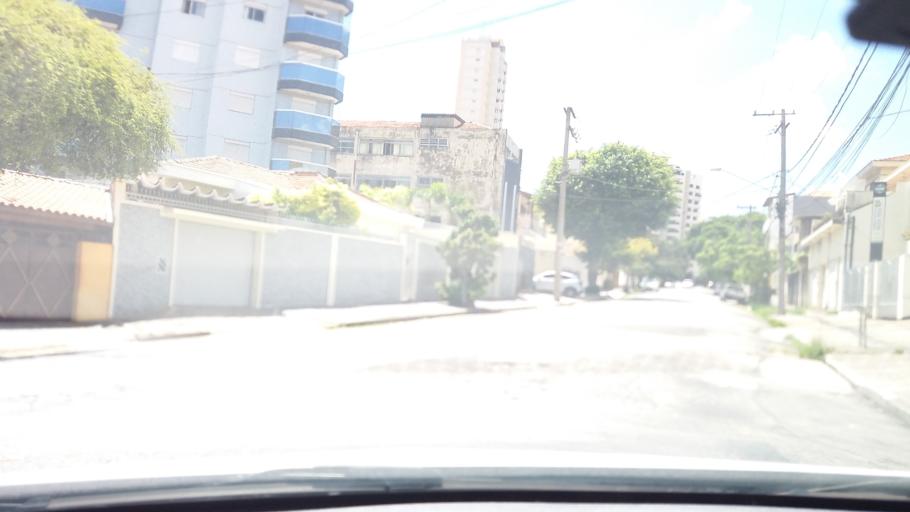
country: BR
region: Sao Paulo
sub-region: Sao Paulo
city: Sao Paulo
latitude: -23.4829
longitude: -46.6212
